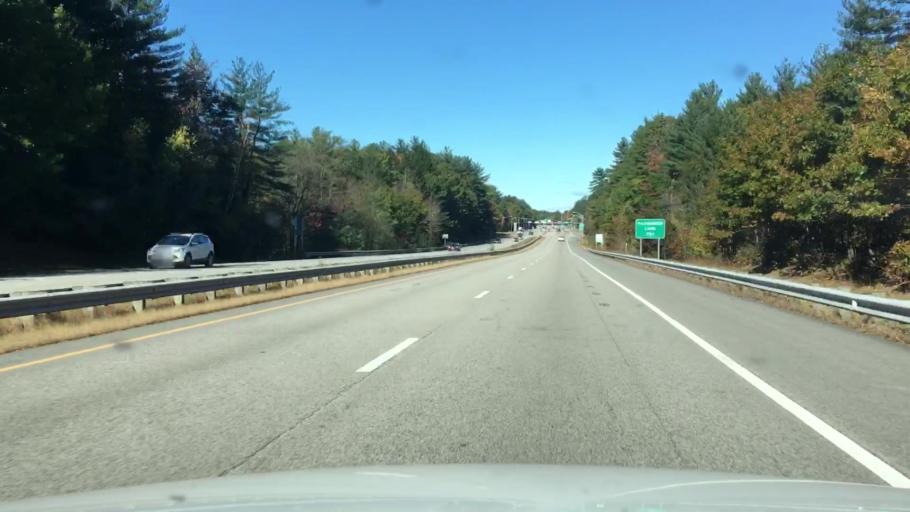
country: US
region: New Hampshire
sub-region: Strafford County
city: Rochester
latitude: 43.2696
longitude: -70.9583
